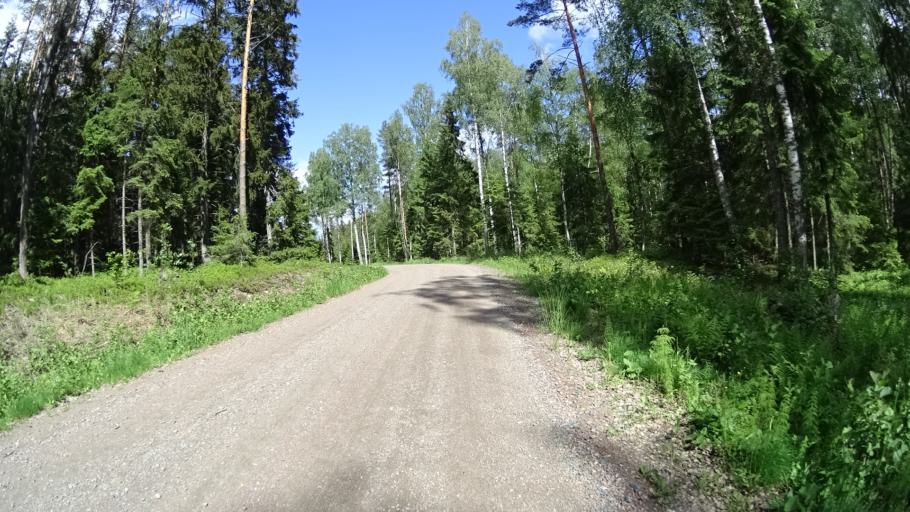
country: FI
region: Uusimaa
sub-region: Raaseporin
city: Karis
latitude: 60.1336
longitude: 23.6206
